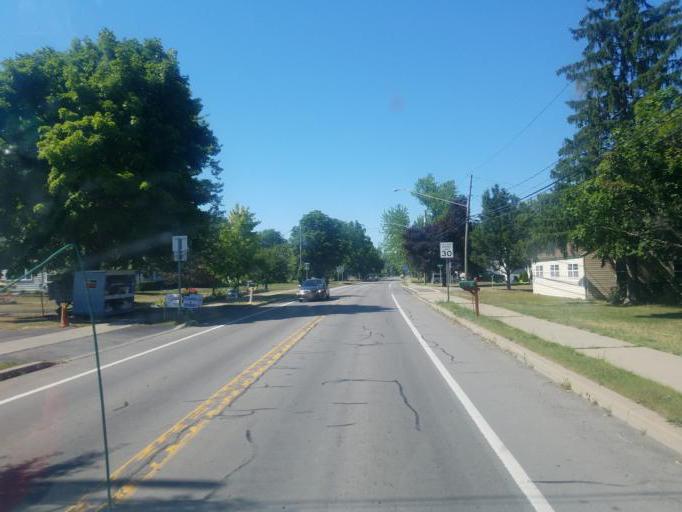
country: US
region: New York
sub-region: Ontario County
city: Phelps
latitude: 42.9633
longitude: -77.0755
